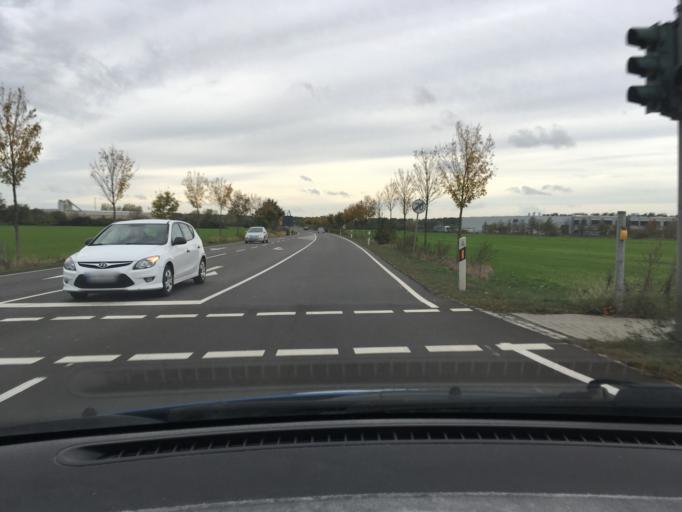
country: DE
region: Saxony-Anhalt
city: Gommern
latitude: 52.0848
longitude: 11.8305
